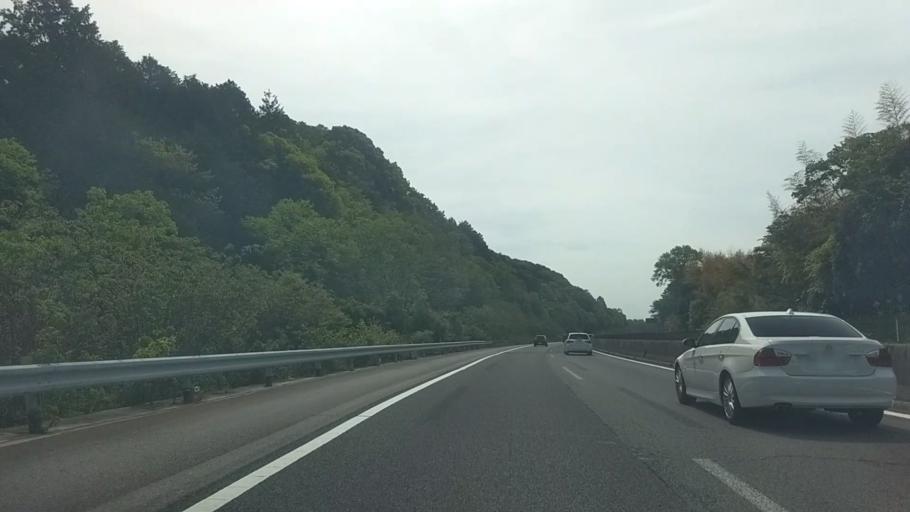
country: JP
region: Aichi
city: Gamagori
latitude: 34.9101
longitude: 137.2461
